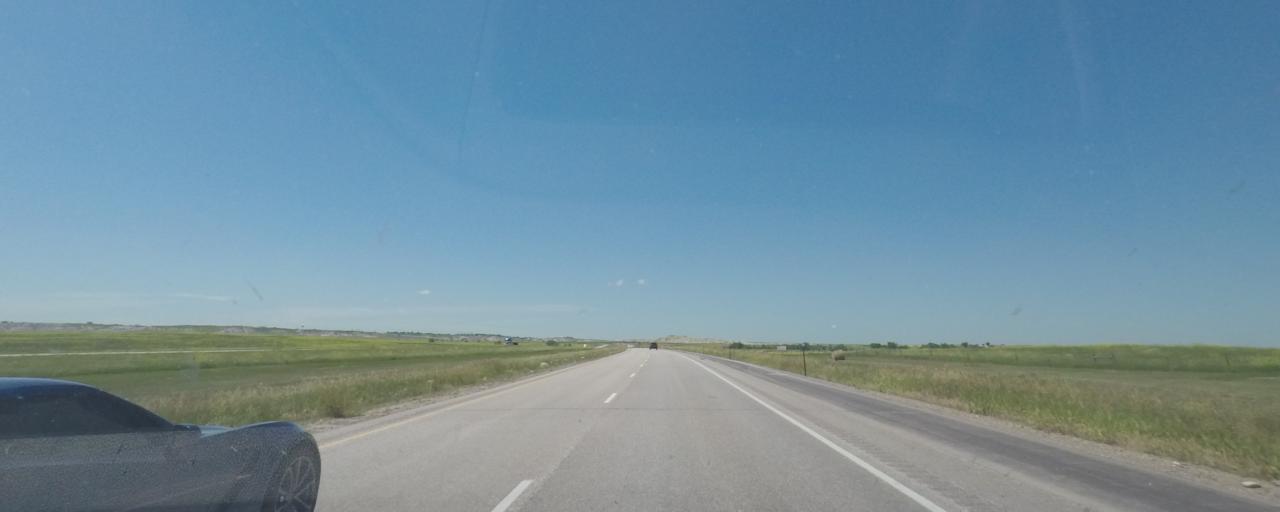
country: US
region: South Dakota
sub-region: Haakon County
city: Philip
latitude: 43.9712
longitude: -102.1877
